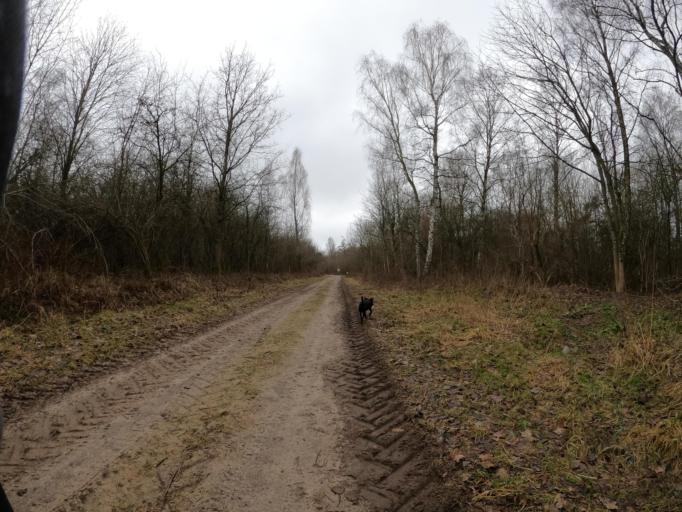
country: PL
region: Greater Poland Voivodeship
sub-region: Powiat zlotowski
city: Sypniewo
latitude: 53.4880
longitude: 16.5648
